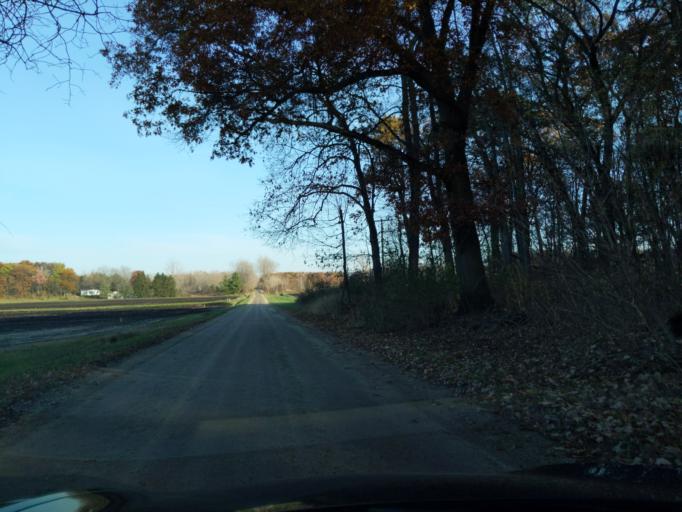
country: US
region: Michigan
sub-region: Clinton County
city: Bath
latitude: 42.7986
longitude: -84.4987
